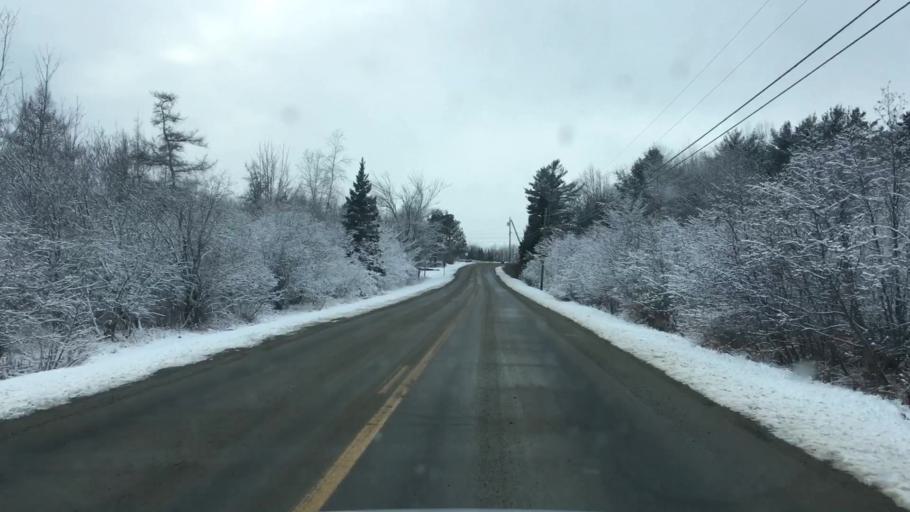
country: US
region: Maine
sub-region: Knox County
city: Owls Head
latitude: 44.0616
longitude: -69.0883
